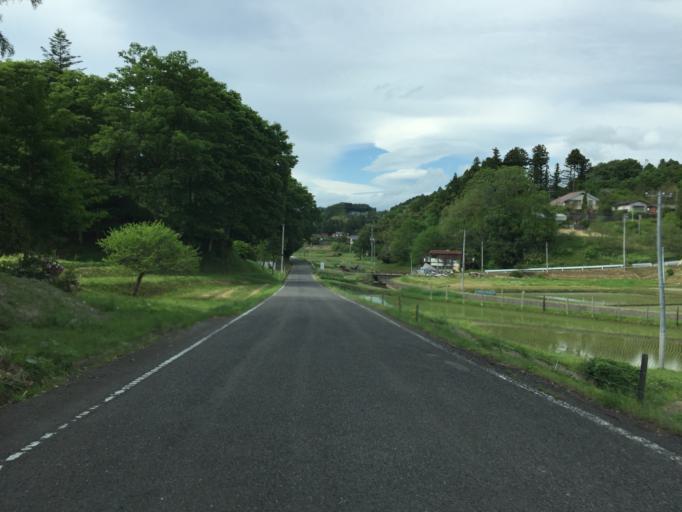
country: JP
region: Fukushima
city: Nihommatsu
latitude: 37.6223
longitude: 140.5322
